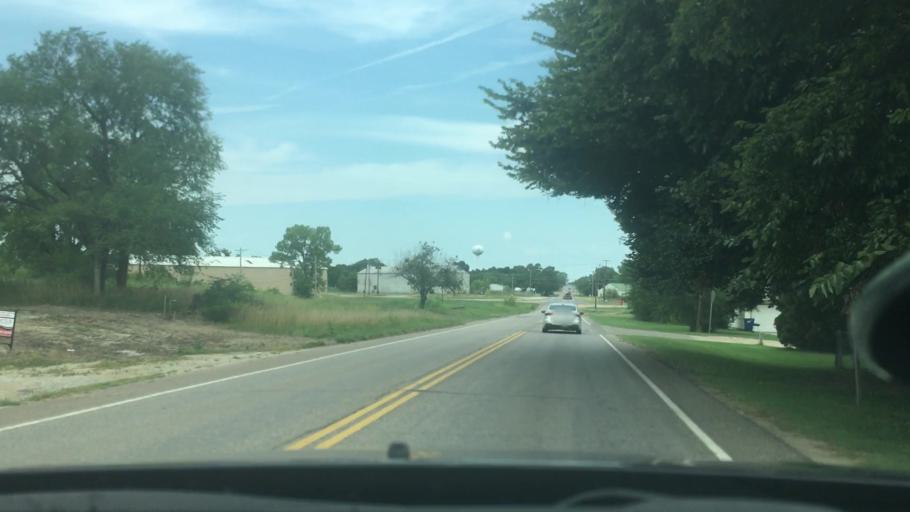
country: US
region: Oklahoma
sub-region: Seminole County
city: Seminole
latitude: 35.2304
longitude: -96.6850
